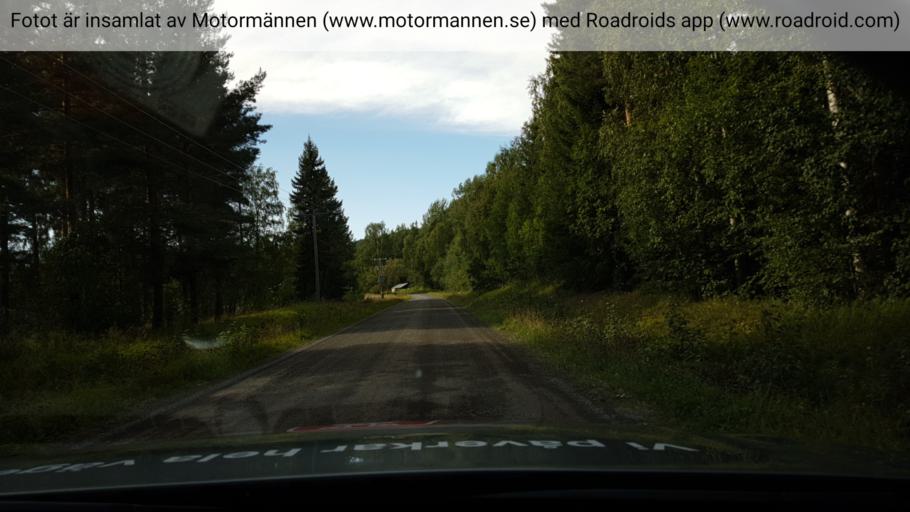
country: SE
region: Jaemtland
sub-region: Braecke Kommun
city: Braecke
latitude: 63.2062
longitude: 15.4049
